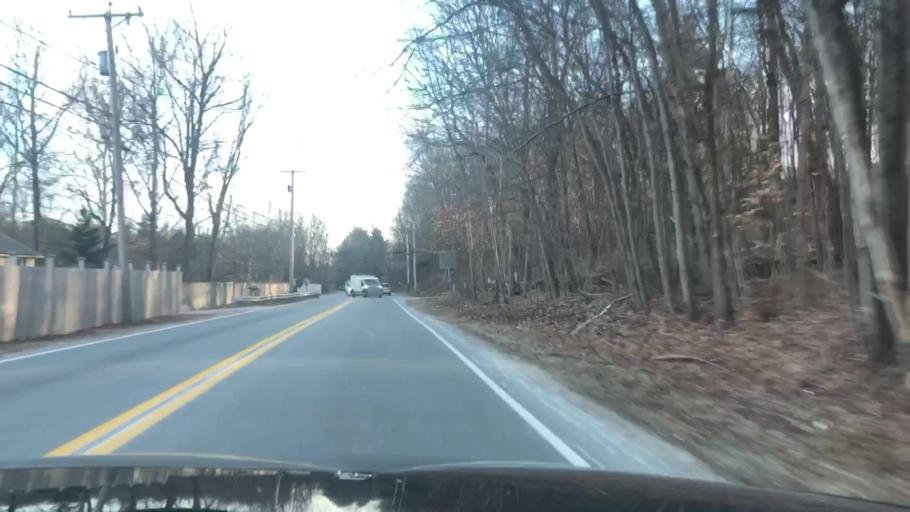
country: US
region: Massachusetts
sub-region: Worcester County
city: Bolton
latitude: 42.4414
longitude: -71.6206
